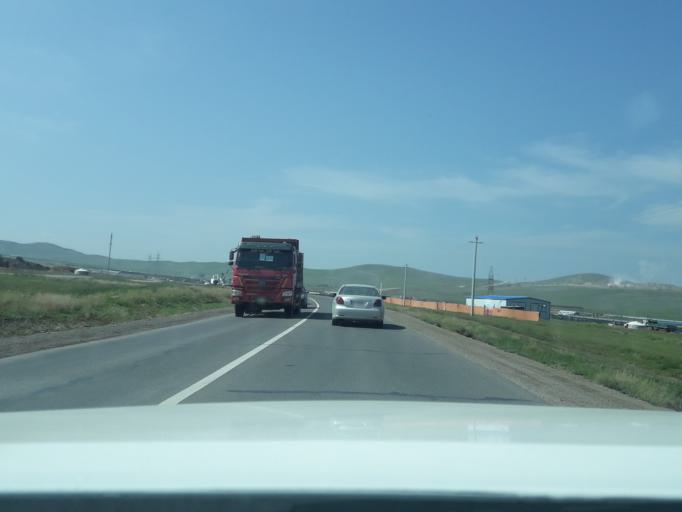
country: MN
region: Ulaanbaatar
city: Ulaanbaatar
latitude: 47.8252
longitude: 106.7676
